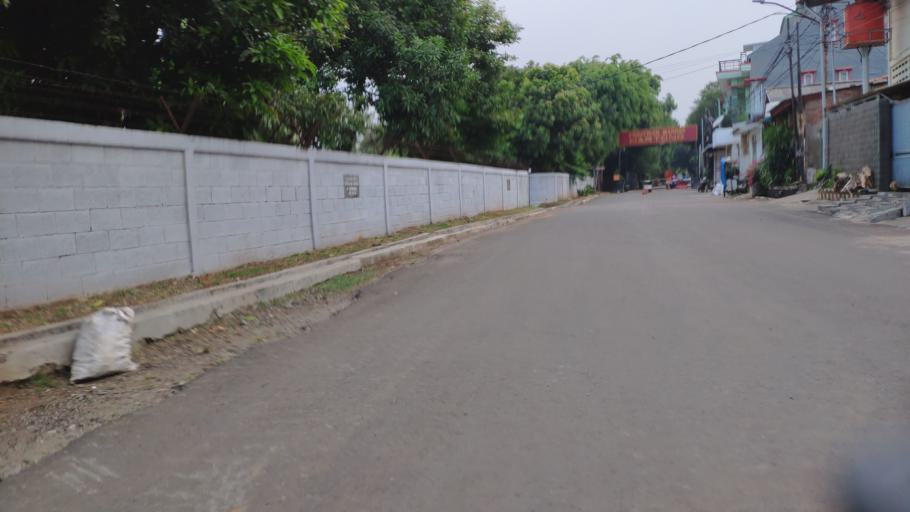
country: ID
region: West Java
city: Pamulang
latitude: -6.2978
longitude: 106.8116
